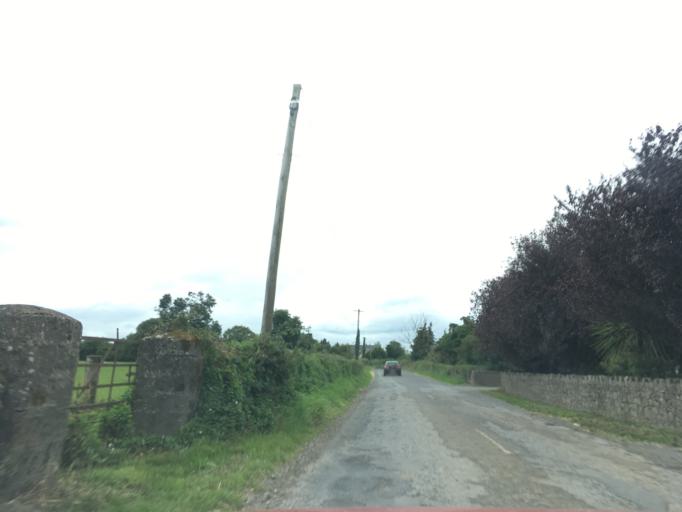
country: IE
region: Munster
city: Cahir
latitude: 52.4584
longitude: -7.9790
